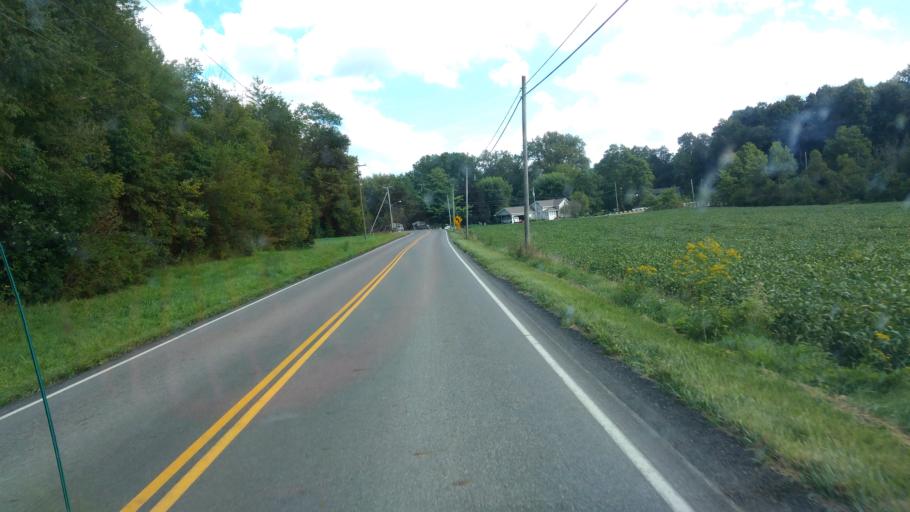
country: US
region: Ohio
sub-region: Holmes County
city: Millersburg
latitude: 40.6066
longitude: -81.8504
